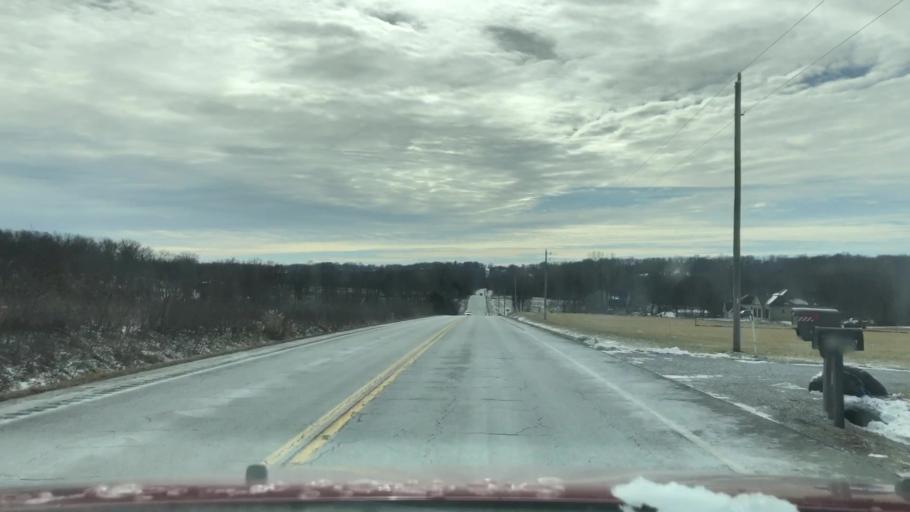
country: US
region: Missouri
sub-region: Jackson County
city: Lone Jack
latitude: 38.9076
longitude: -94.1335
